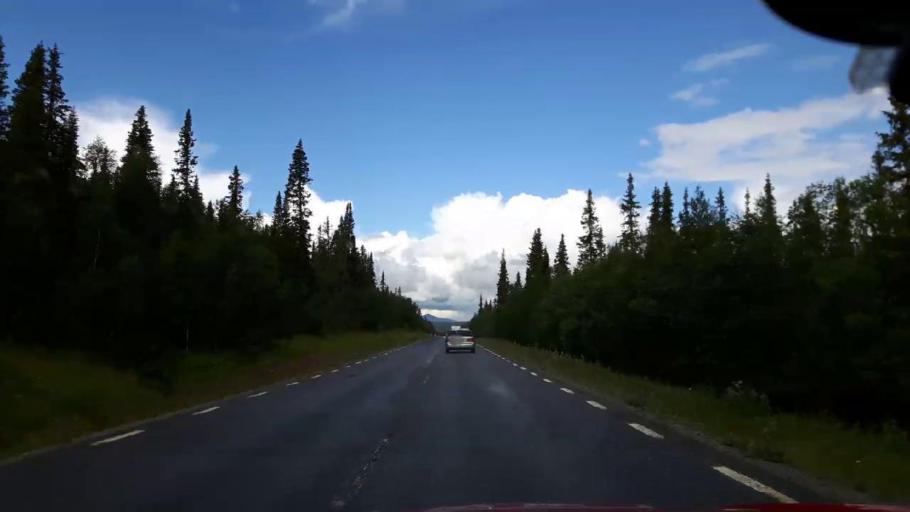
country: SE
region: Vaesterbotten
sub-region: Vilhelmina Kommun
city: Sjoberg
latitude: 65.0267
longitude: 15.1480
